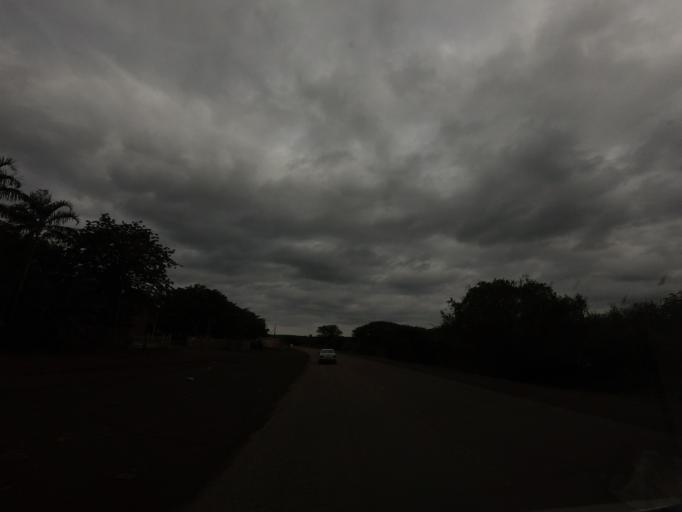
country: ZA
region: Mpumalanga
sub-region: Ehlanzeni District
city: Komatipoort
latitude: -25.4465
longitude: 31.9528
